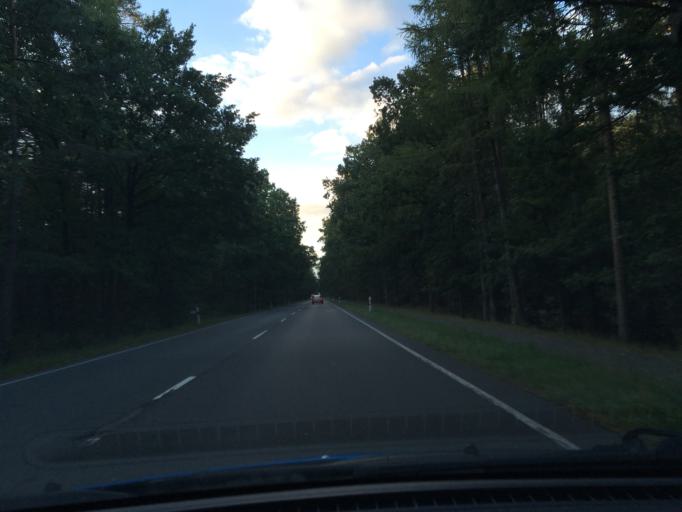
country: DE
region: Lower Saxony
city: Bergen
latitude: 52.7498
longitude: 9.9780
